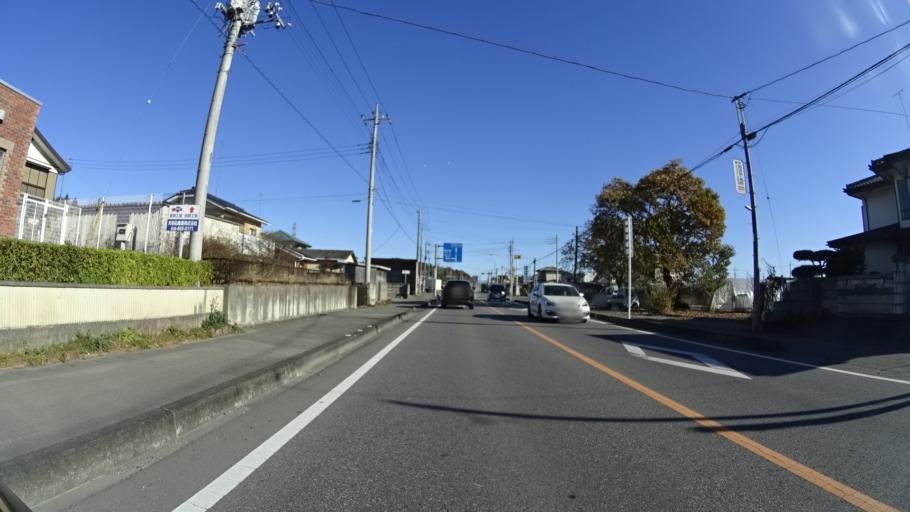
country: JP
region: Tochigi
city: Utsunomiya-shi
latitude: 36.5948
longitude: 139.8069
